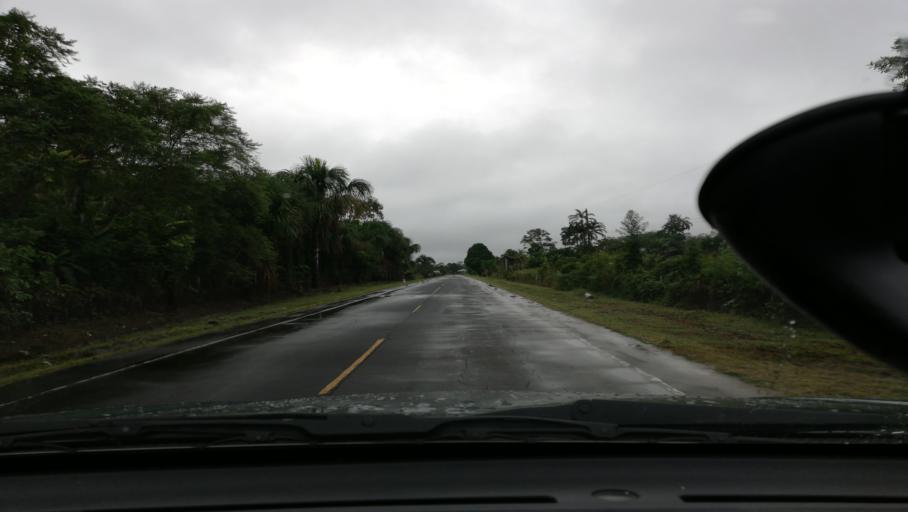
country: PE
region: Loreto
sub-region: Provincia de Maynas
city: San Juan
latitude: -4.1082
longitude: -73.4578
